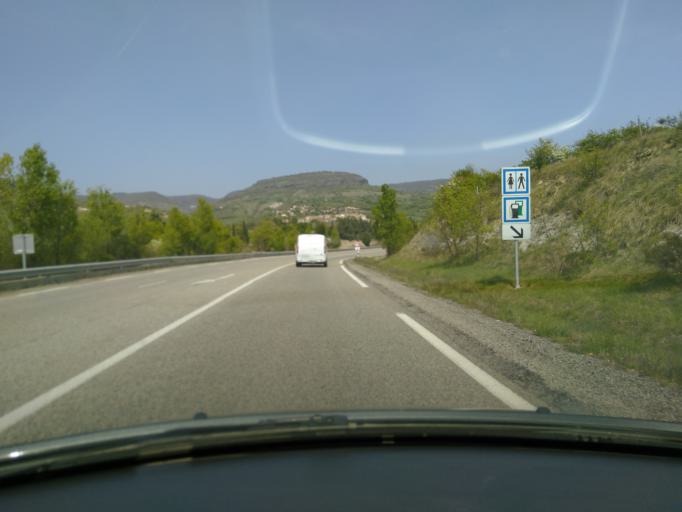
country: FR
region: Rhone-Alpes
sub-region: Departement de l'Ardeche
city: Villeneuve-de-Berg
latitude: 44.5818
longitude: 4.5286
